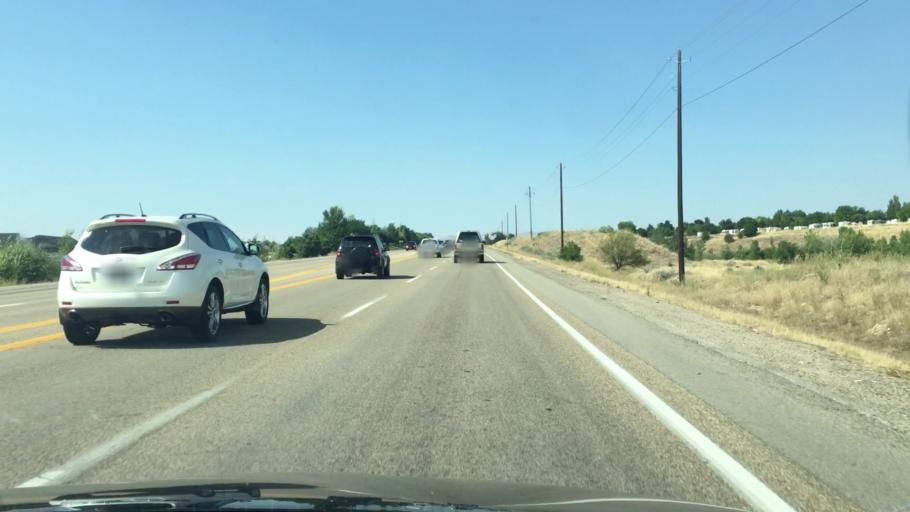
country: US
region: Idaho
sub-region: Ada County
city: Eagle
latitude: 43.6940
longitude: -116.3191
